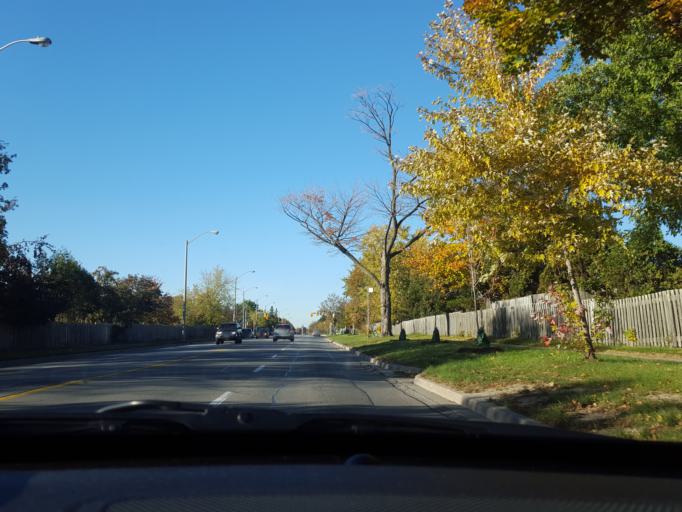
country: CA
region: Ontario
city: Markham
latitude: 43.8198
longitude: -79.2836
